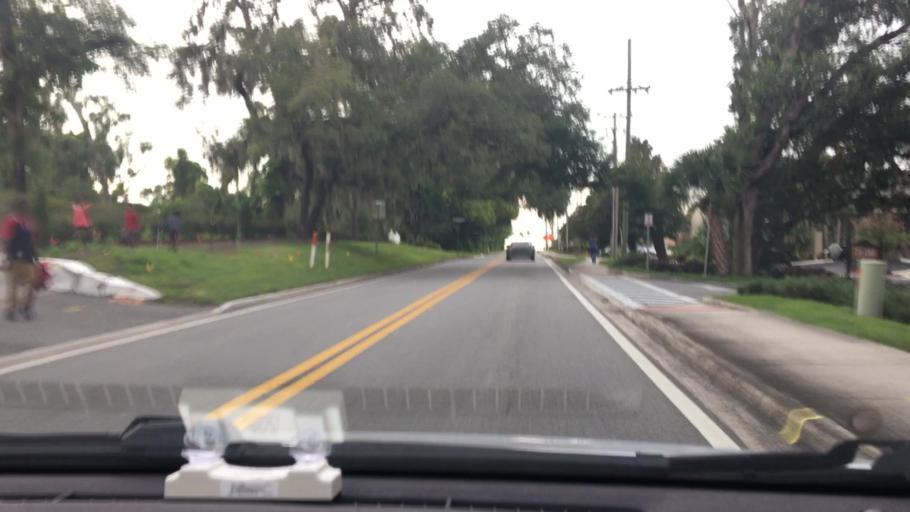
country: US
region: Florida
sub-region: Seminole County
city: Altamonte Springs
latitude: 28.6536
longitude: -81.3904
